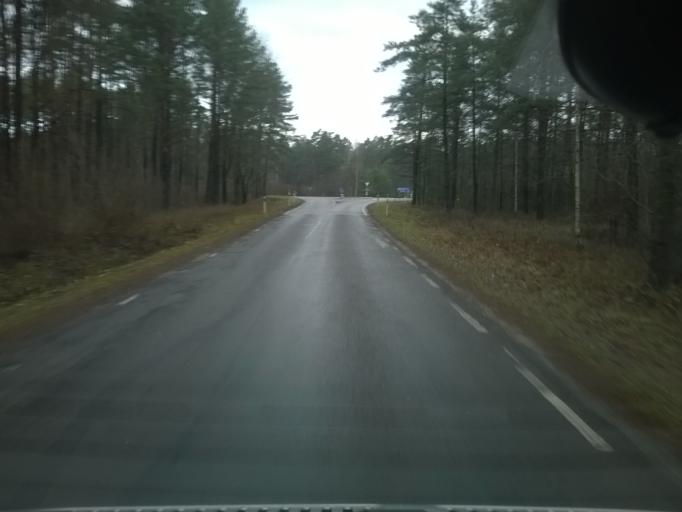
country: EE
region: Laeaene
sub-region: Ridala Parish
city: Uuemoisa
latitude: 58.9557
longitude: 23.7251
